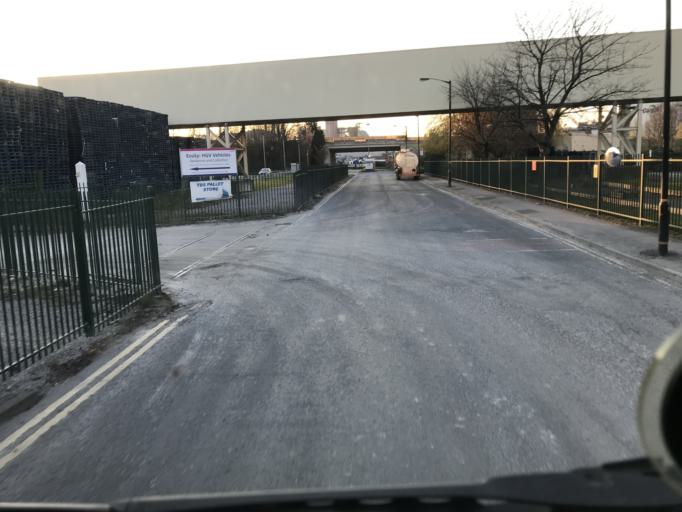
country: GB
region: England
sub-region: City and Borough of Salford
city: Eccles
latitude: 53.4769
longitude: -2.3226
